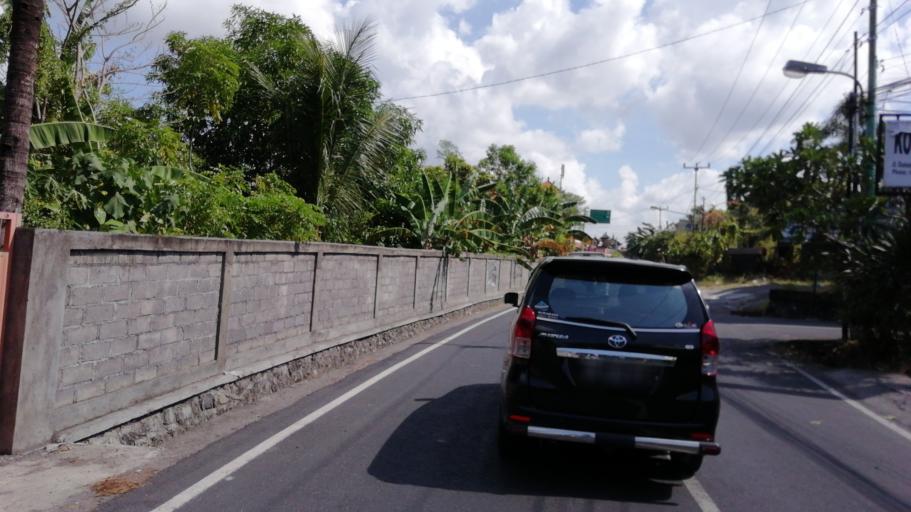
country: ID
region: Bali
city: Denpasar
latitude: -8.6735
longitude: 115.1728
